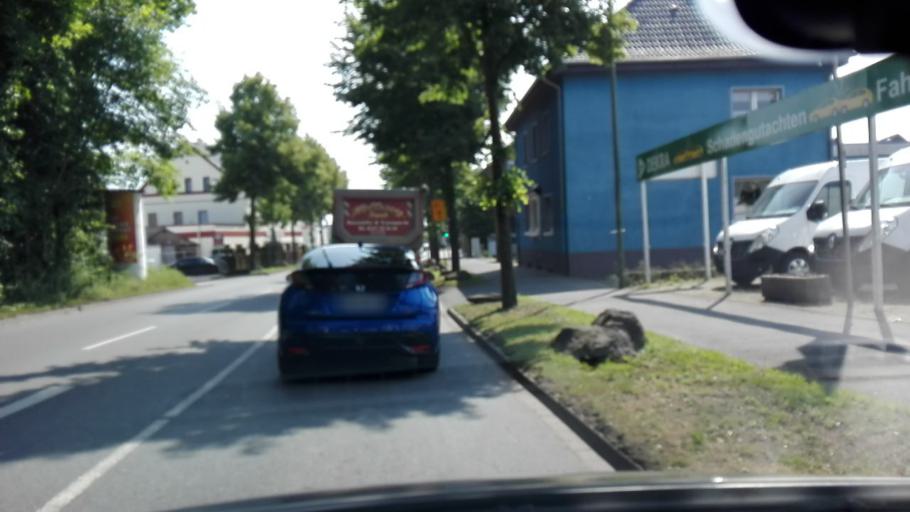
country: DE
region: North Rhine-Westphalia
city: Lunen
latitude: 51.6121
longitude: 7.5611
